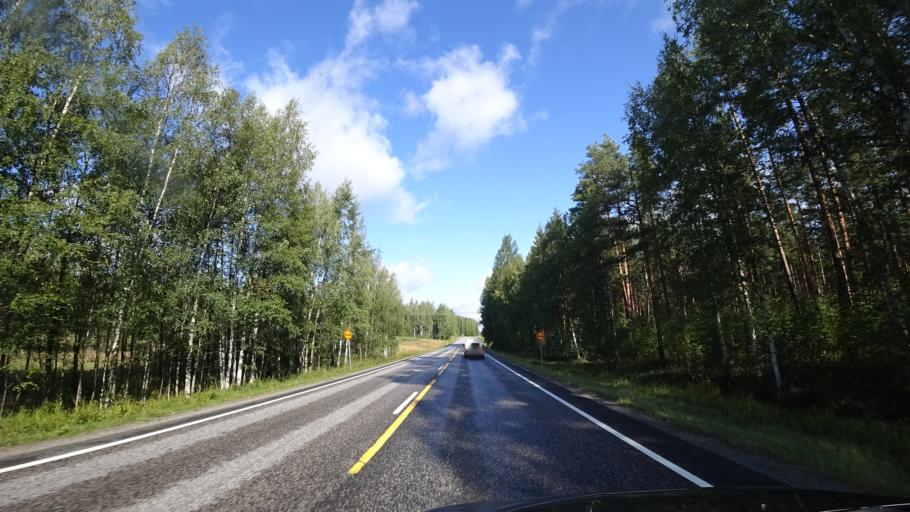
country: FI
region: Uusimaa
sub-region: Helsinki
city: Tuusula
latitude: 60.4562
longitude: 24.9521
